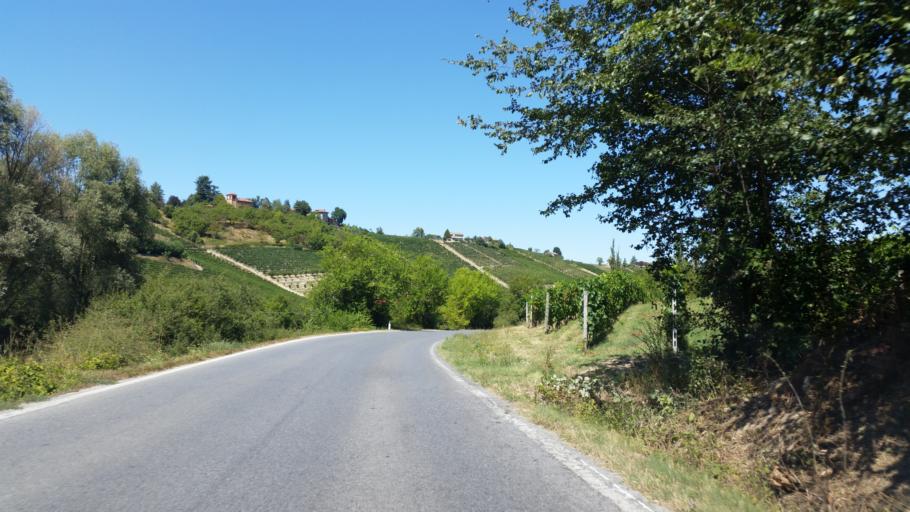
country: IT
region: Piedmont
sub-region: Provincia di Cuneo
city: Alba
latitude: 44.6936
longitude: 8.0529
